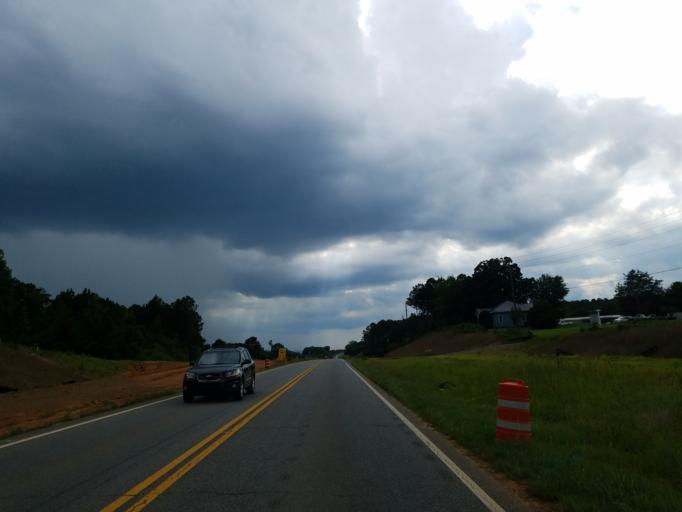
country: US
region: Georgia
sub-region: Floyd County
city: Shannon
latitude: 34.3686
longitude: -85.0256
